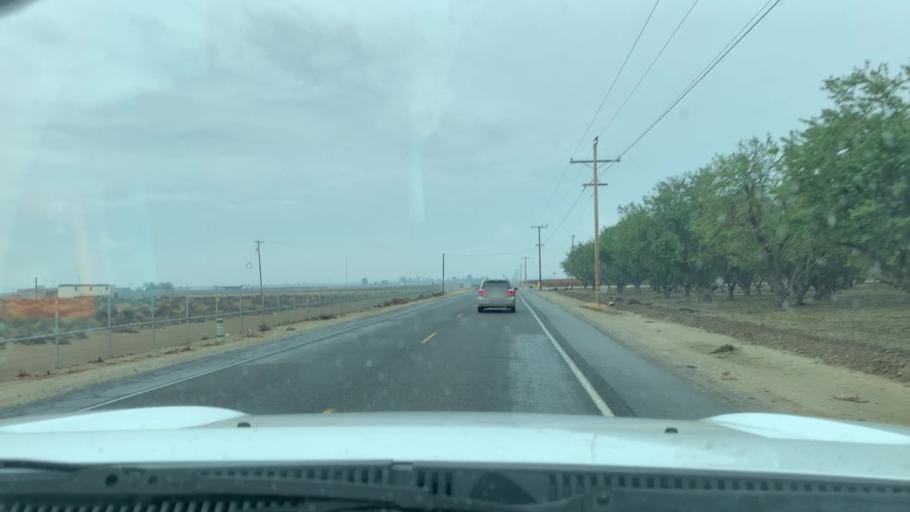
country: US
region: California
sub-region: Kern County
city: Delano
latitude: 35.7613
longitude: -119.3136
